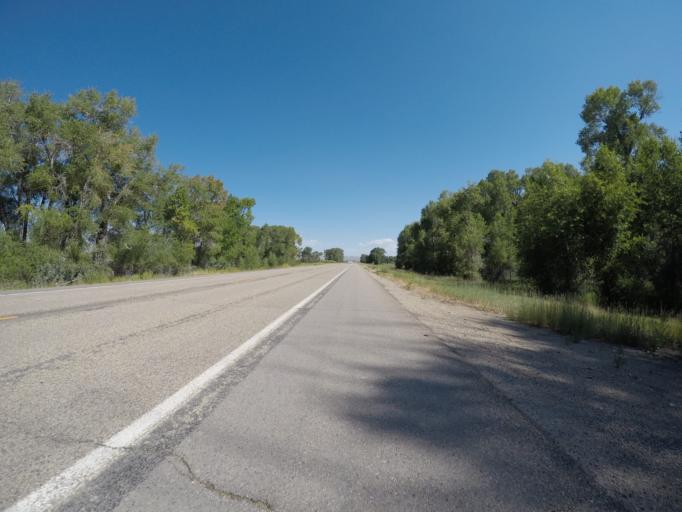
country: US
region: Wyoming
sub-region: Sublette County
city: Marbleton
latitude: 42.2216
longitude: -110.1909
